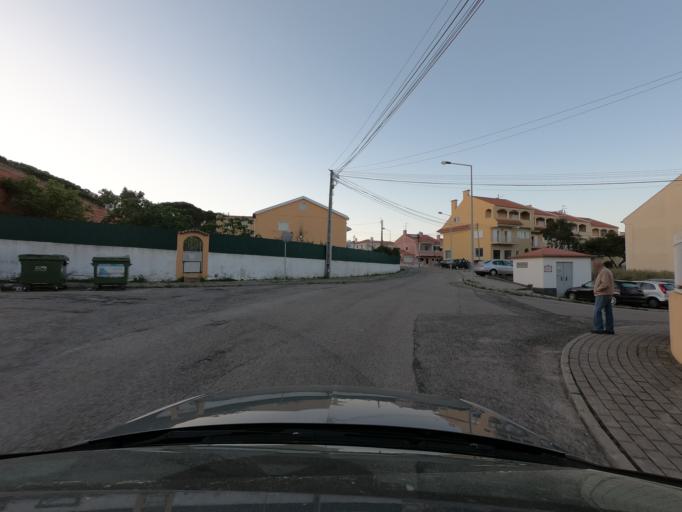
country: PT
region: Lisbon
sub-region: Sintra
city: Rio de Mouro
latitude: 38.7557
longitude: -9.3550
